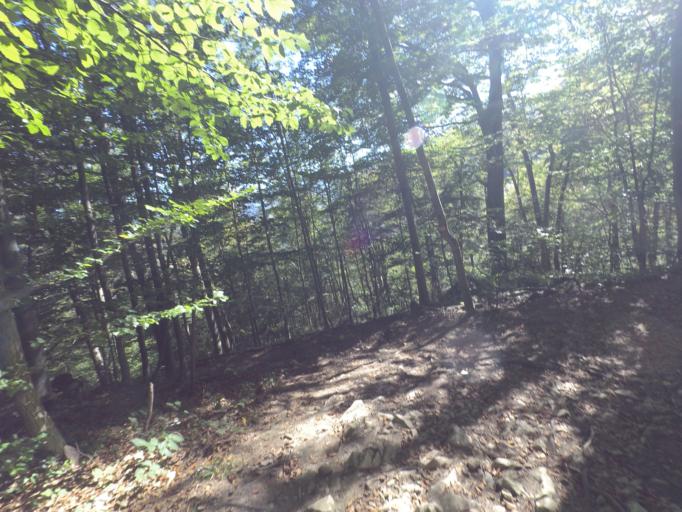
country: AT
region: Salzburg
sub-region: Politischer Bezirk Hallein
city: Hallein
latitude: 47.6824
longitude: 13.0873
